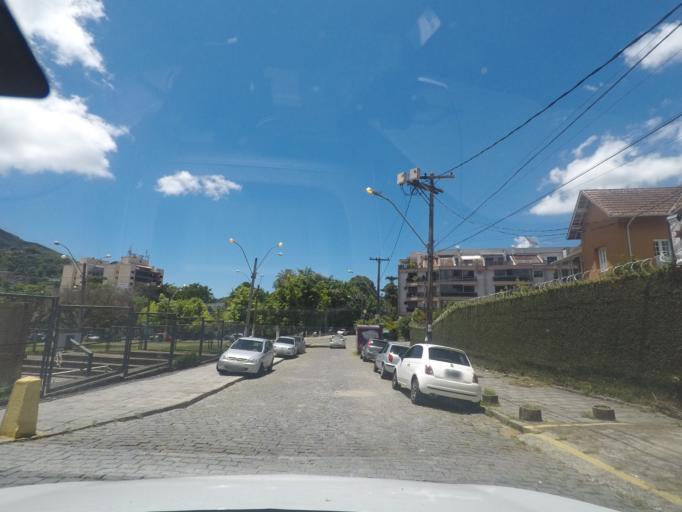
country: BR
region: Rio de Janeiro
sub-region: Teresopolis
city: Teresopolis
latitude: -22.4346
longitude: -42.9797
